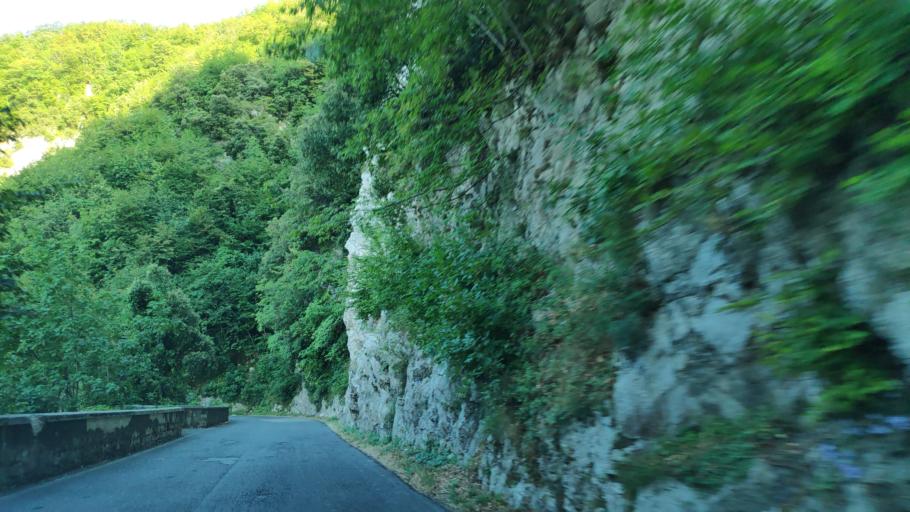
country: IT
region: Campania
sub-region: Provincia di Salerno
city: Pietre
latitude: 40.7182
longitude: 14.6115
